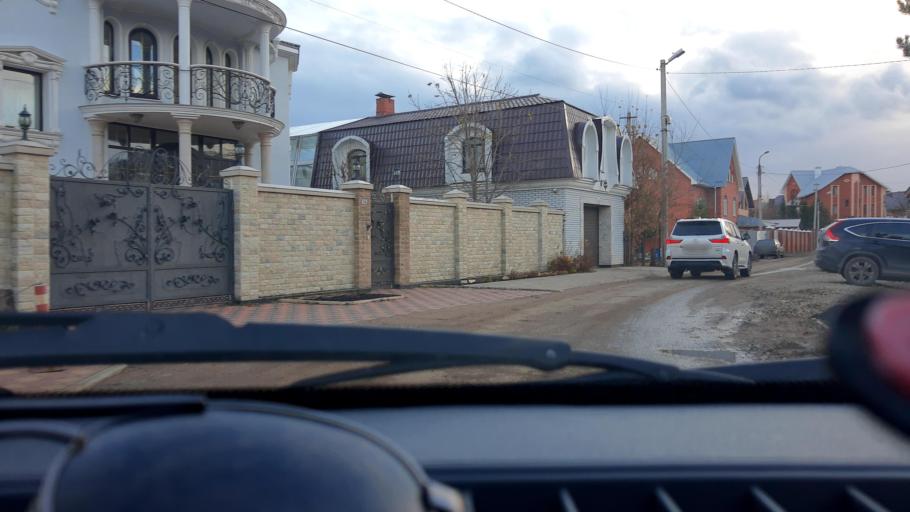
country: RU
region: Bashkortostan
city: Ufa
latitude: 54.6900
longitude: 55.9774
